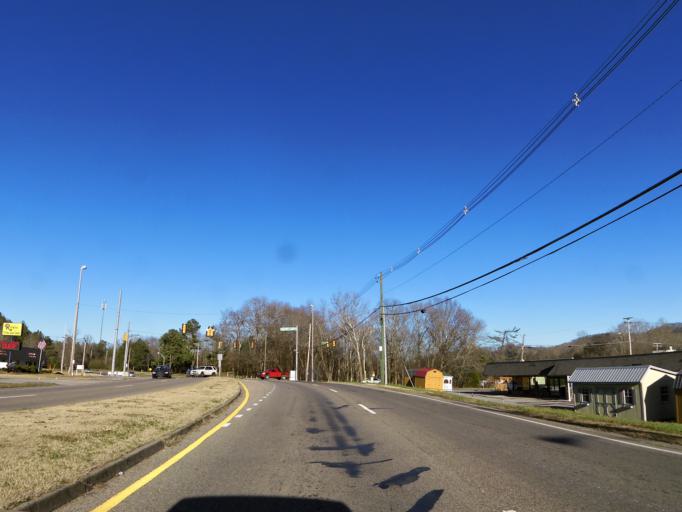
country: US
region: Tennessee
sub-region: Anderson County
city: Oak Ridge
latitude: 36.0457
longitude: -84.2087
